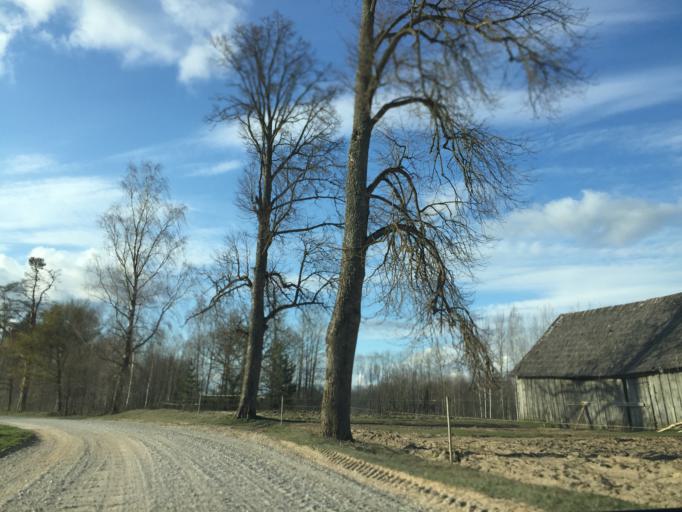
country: LV
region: Burtnieki
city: Matisi
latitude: 57.6079
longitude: 25.0779
